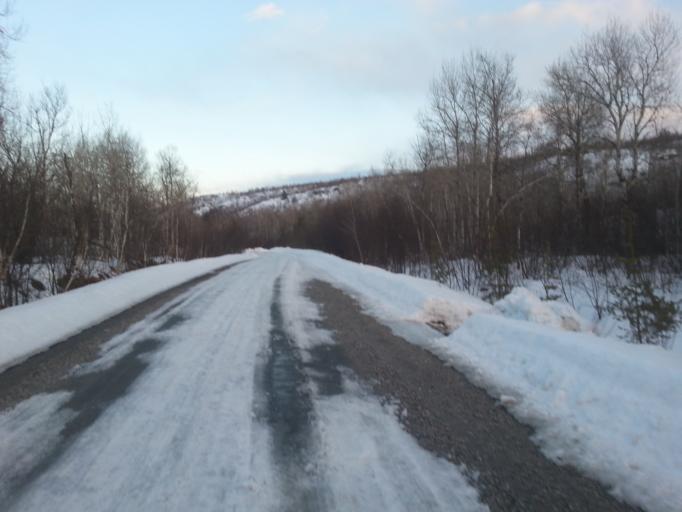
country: CA
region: Ontario
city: Greater Sudbury
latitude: 46.5908
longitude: -80.9976
